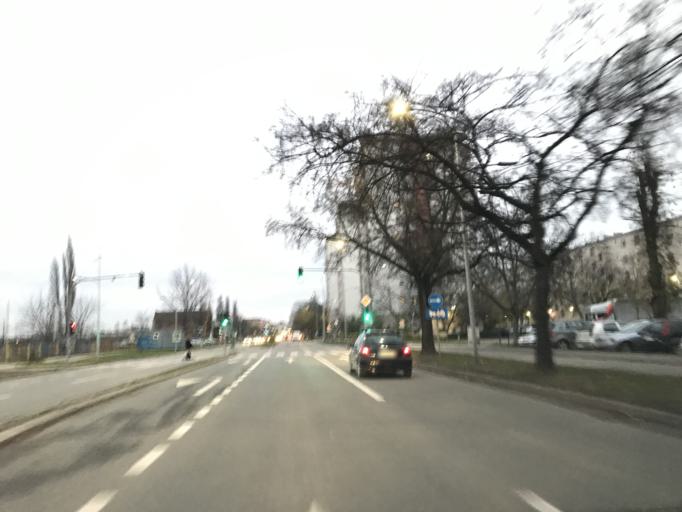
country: RS
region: Autonomna Pokrajina Vojvodina
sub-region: Juznobacki Okrug
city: Novi Sad
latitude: 45.2680
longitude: 19.8119
